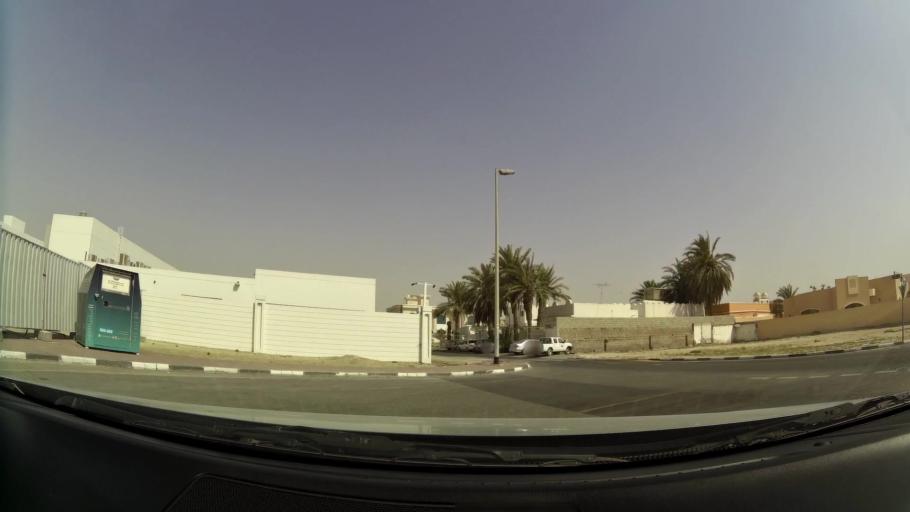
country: AE
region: Dubai
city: Dubai
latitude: 25.1668
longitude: 55.2578
